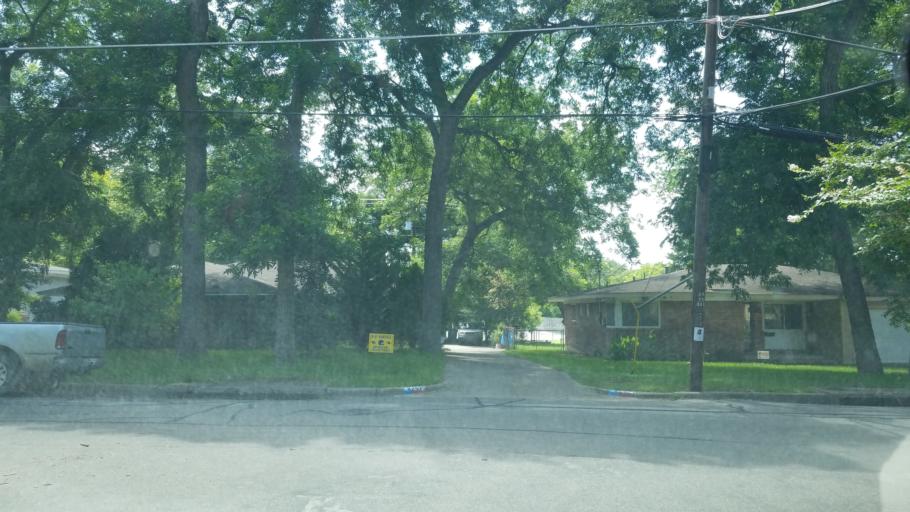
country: US
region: Texas
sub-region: Dallas County
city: Balch Springs
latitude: 32.7564
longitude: -96.6994
